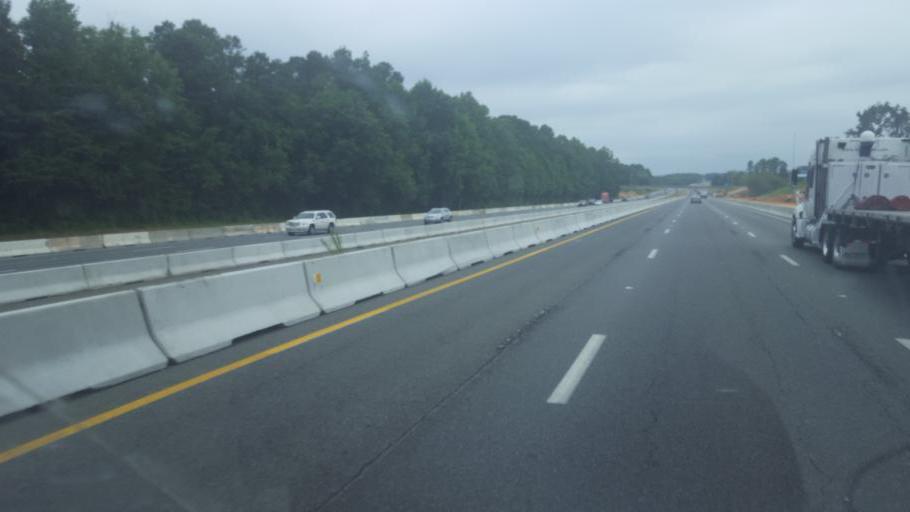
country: US
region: North Carolina
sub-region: Mecklenburg County
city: Huntersville
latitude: 35.3286
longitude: -80.8481
